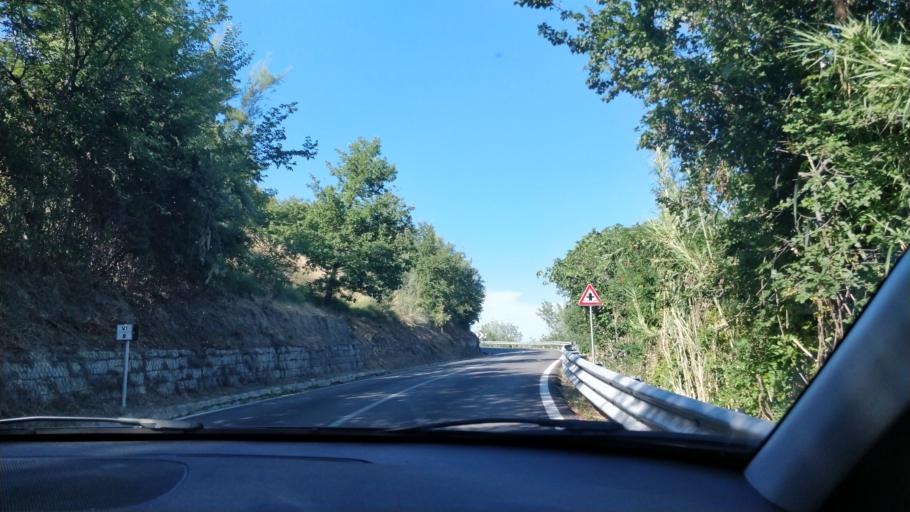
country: IT
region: Abruzzo
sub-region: Provincia di Pescara
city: Serramonacesca
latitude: 42.2543
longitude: 14.0897
